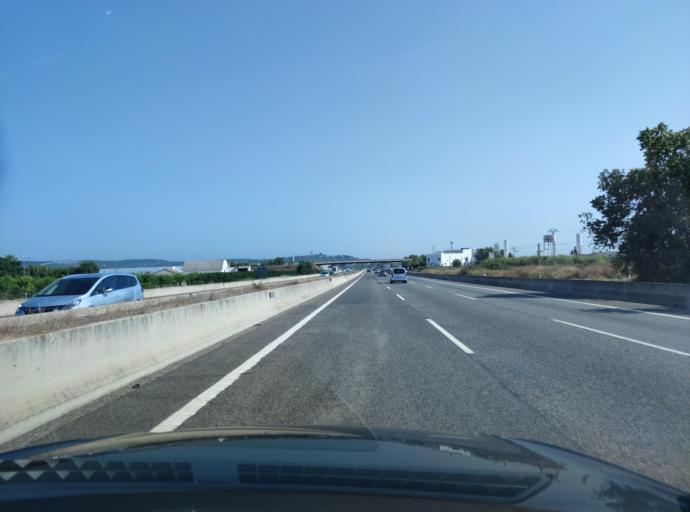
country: ES
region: Valencia
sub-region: Provincia de Valencia
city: Beneixida
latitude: 39.0620
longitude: -0.5432
